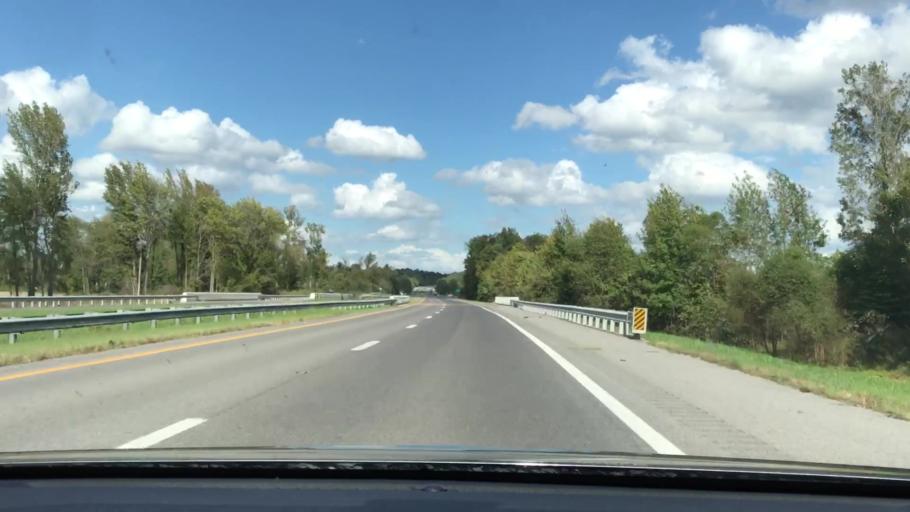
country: US
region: Kentucky
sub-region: Marshall County
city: Benton
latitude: 36.8045
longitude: -88.4951
